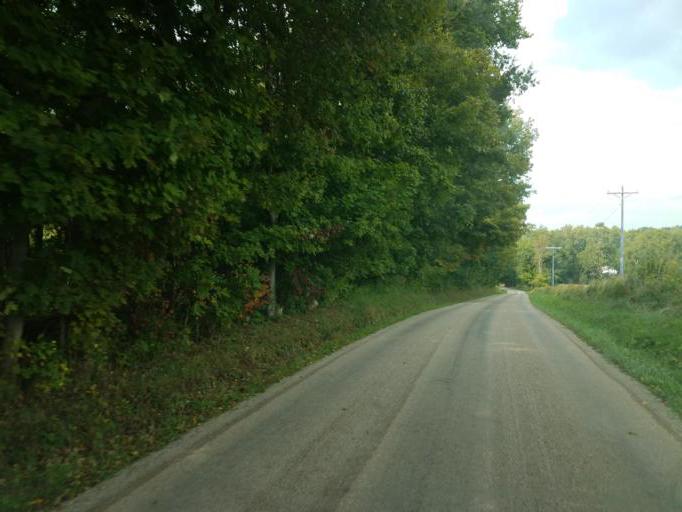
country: US
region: Ohio
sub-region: Knox County
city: Gambier
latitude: 40.3421
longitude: -82.3876
